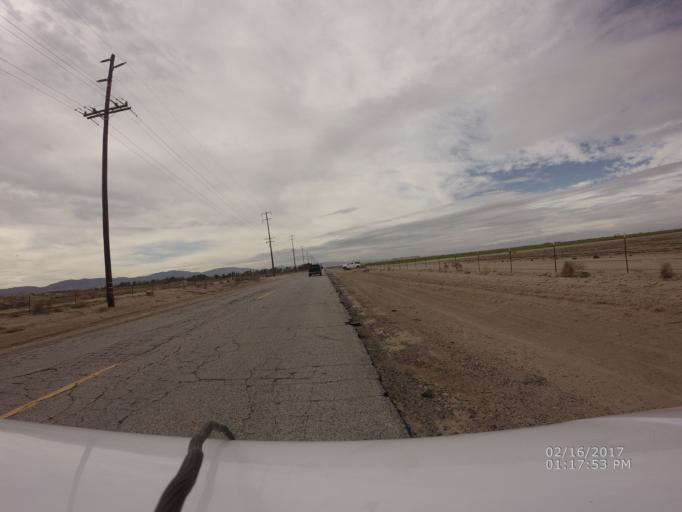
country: US
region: California
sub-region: Los Angeles County
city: Palmdale
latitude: 34.6313
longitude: -118.0313
